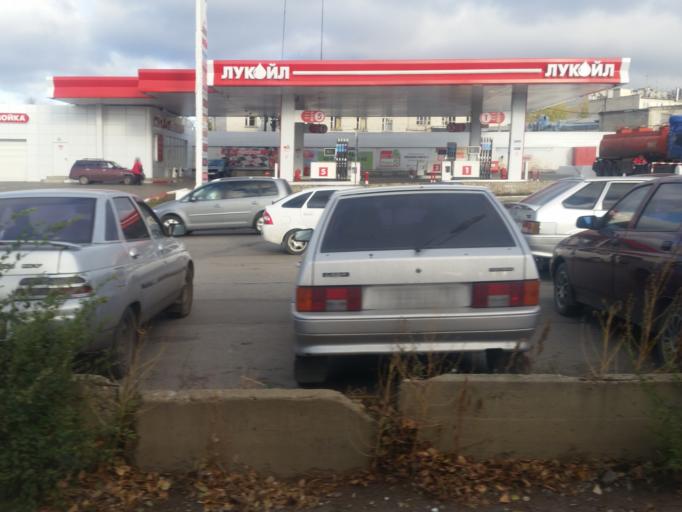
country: RU
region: Ulyanovsk
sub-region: Ulyanovskiy Rayon
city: Ulyanovsk
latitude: 54.3165
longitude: 48.3855
